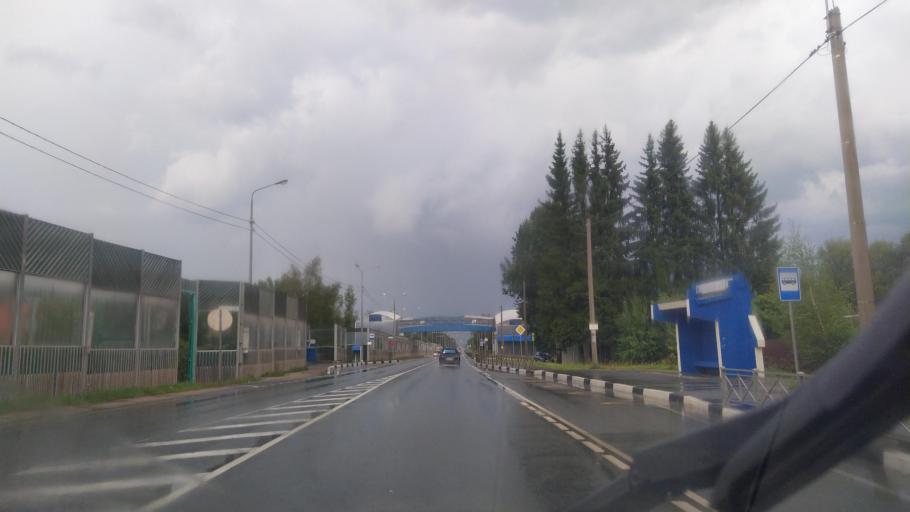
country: RU
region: Pskov
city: Pskov
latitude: 57.7589
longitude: 28.3842
